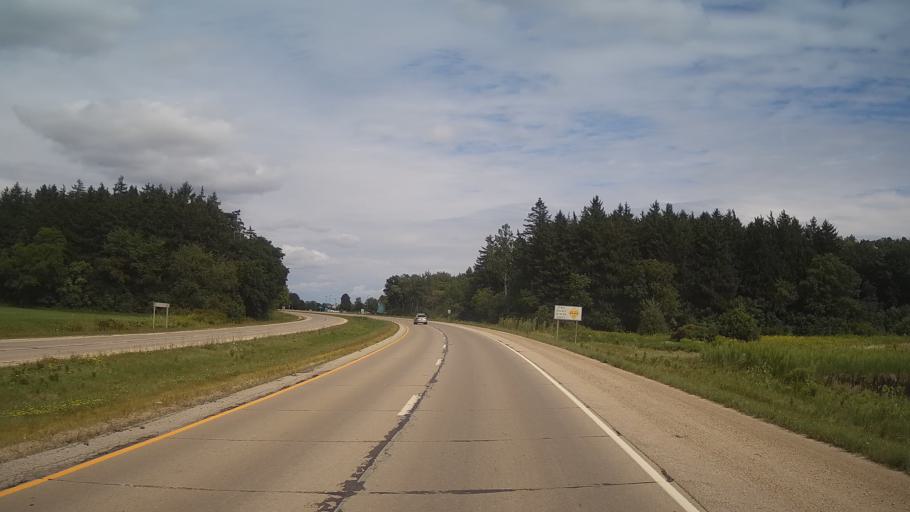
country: US
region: Wisconsin
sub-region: Winnebago County
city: Oshkosh
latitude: 44.0282
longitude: -88.6017
